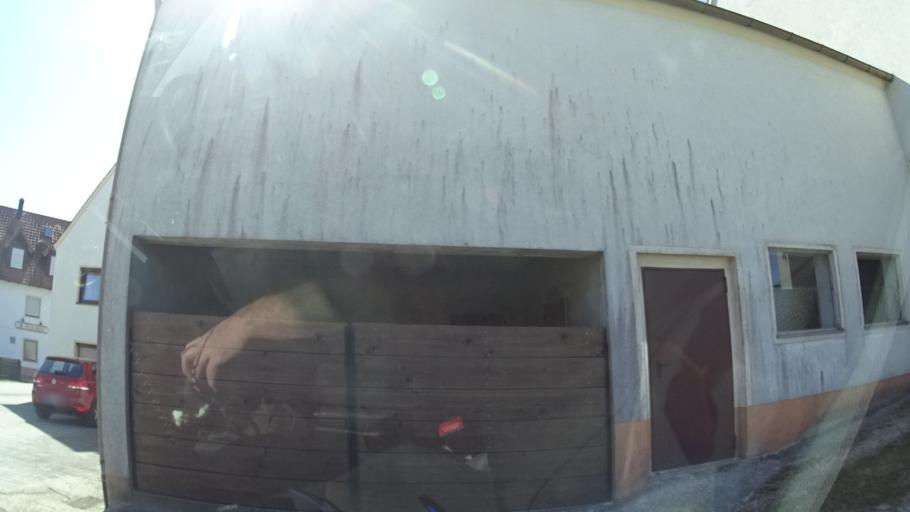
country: DE
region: Bavaria
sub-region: Regierungsbezirk Mittelfranken
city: Alfeld
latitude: 49.4251
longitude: 11.5018
